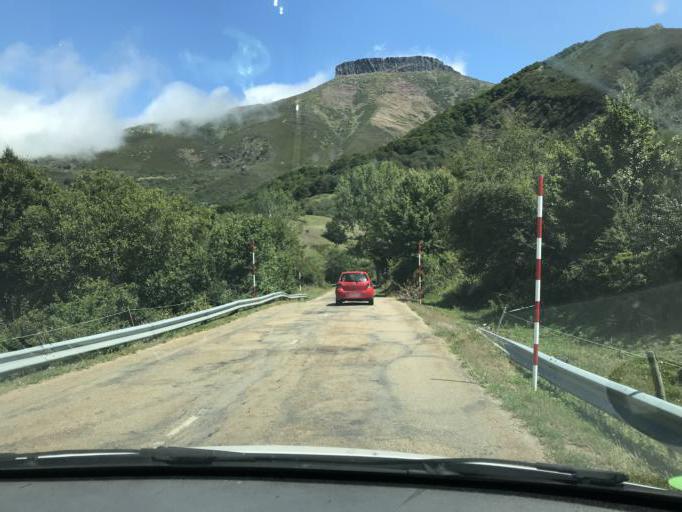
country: ES
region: Castille and Leon
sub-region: Provincia de Palencia
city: Polentinos
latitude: 43.0437
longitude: -4.4551
